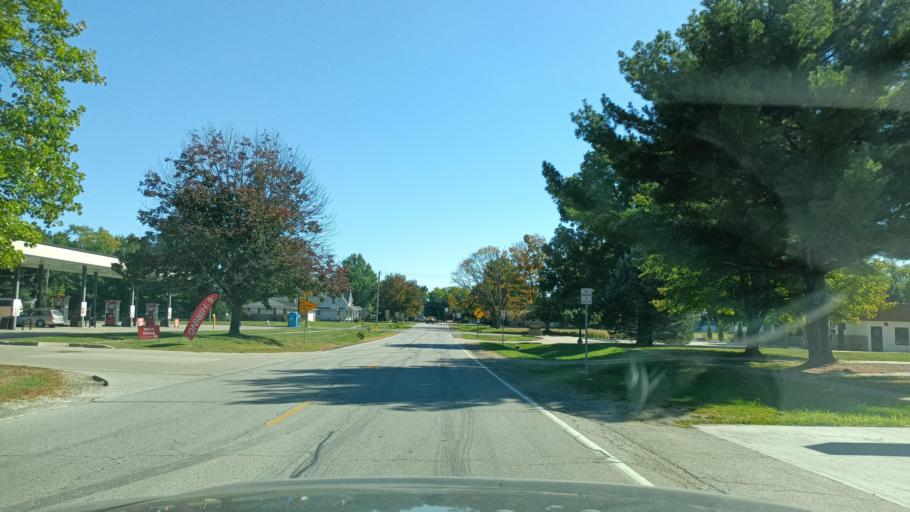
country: US
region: Illinois
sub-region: Peoria County
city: Elmwood
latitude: 40.8388
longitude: -89.8827
